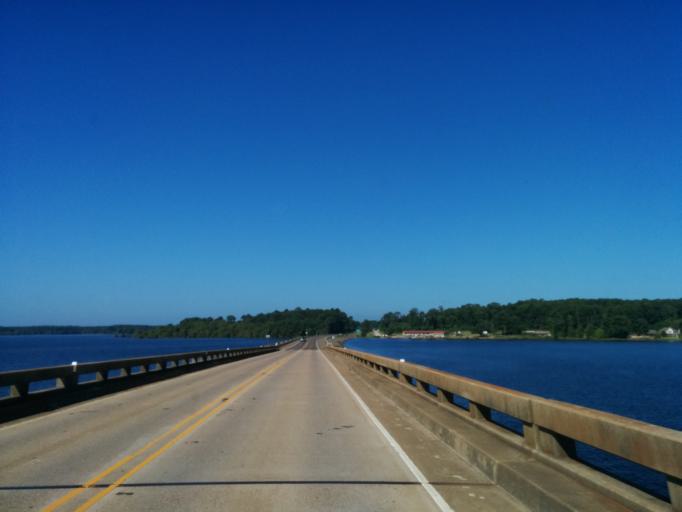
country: US
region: Texas
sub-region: Sabine County
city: Milam
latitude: 31.4665
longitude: -93.7450
